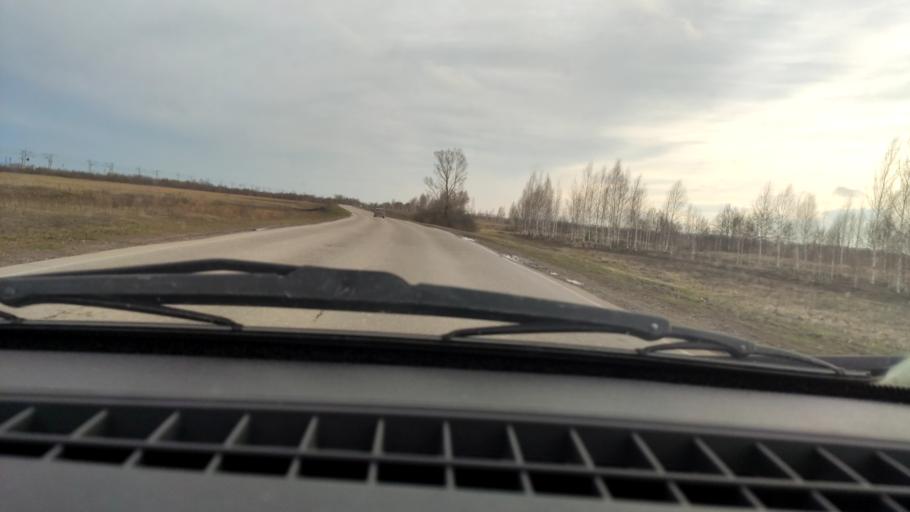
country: RU
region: Bashkortostan
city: Chishmy
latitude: 54.4352
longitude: 55.2360
